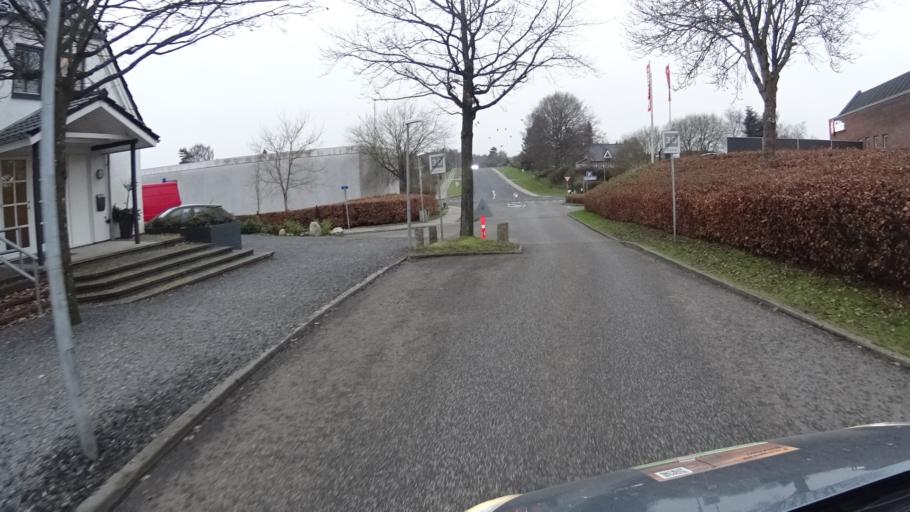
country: DK
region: South Denmark
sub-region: Vejle Kommune
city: Vejle
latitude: 55.7189
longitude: 9.6074
